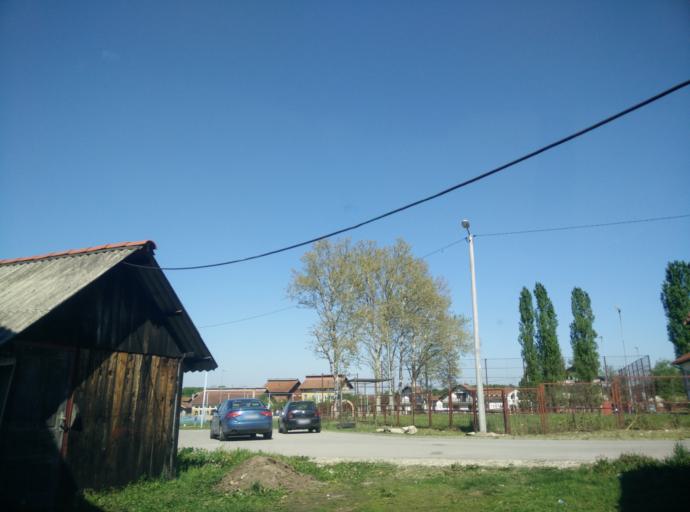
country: BA
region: Brcko
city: Brcko
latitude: 44.8423
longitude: 18.8184
